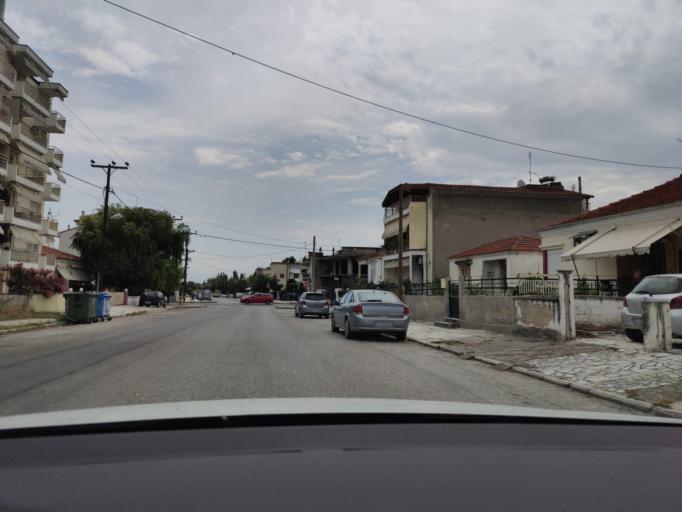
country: GR
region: Central Macedonia
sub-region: Nomos Serron
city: Serres
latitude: 41.0820
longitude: 23.5362
